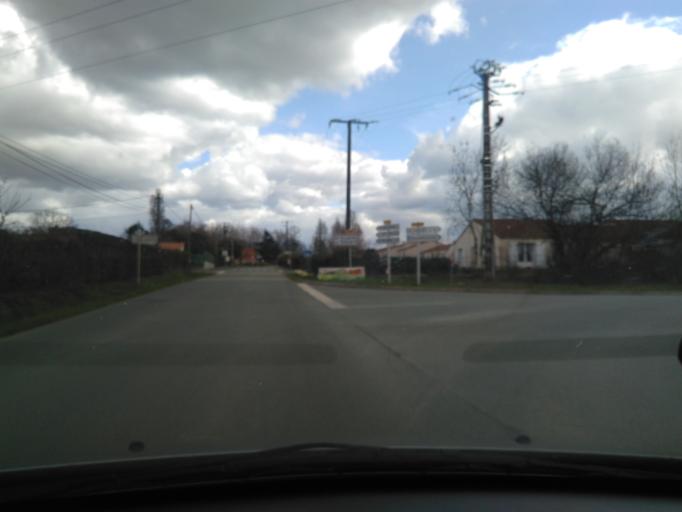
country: FR
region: Pays de la Loire
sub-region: Departement de la Vendee
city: Saint-Martin-des-Noyers
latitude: 46.6916
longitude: -1.1325
